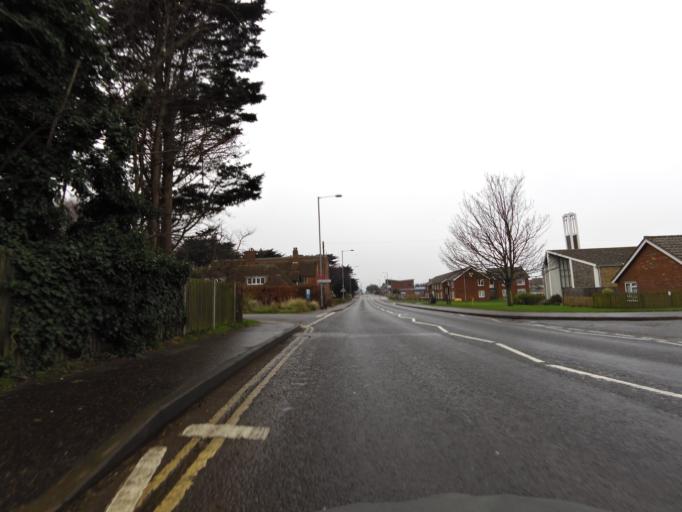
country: GB
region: England
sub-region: Norfolk
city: Sheringham
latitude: 52.9401
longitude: 1.2136
